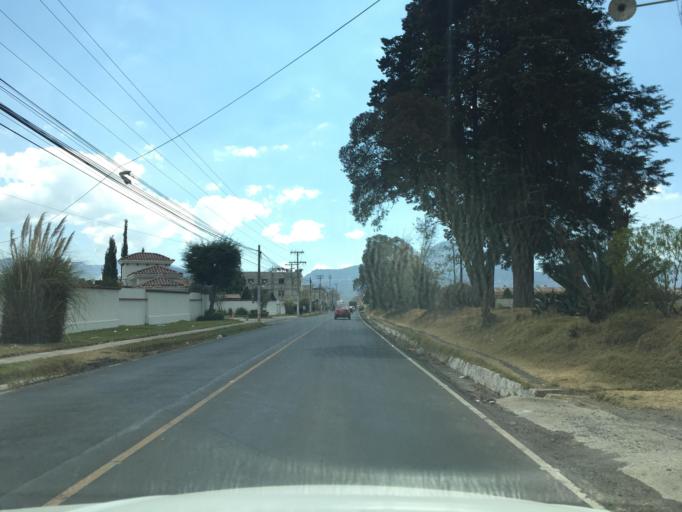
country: GT
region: Quetzaltenango
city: Olintepeque
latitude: 14.8687
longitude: -91.5129
